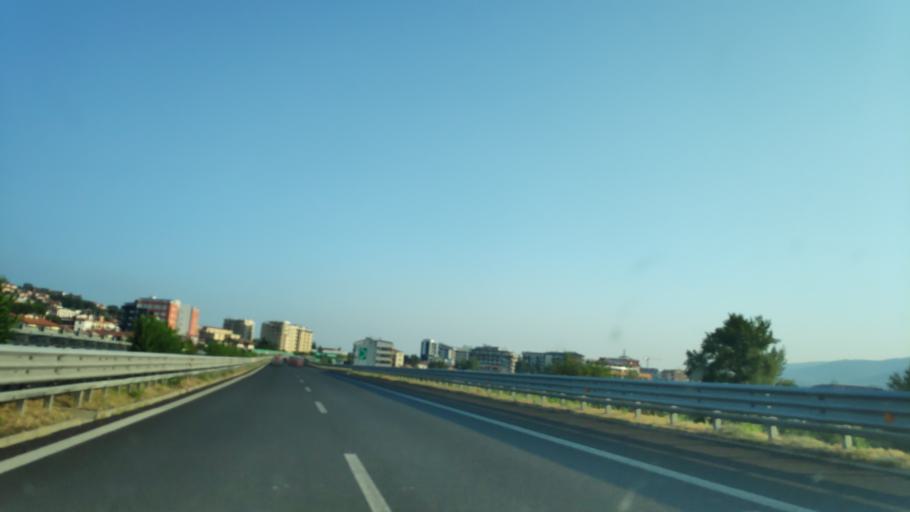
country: IT
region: Calabria
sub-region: Provincia di Cosenza
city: Cosenza
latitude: 39.3192
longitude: 16.2411
